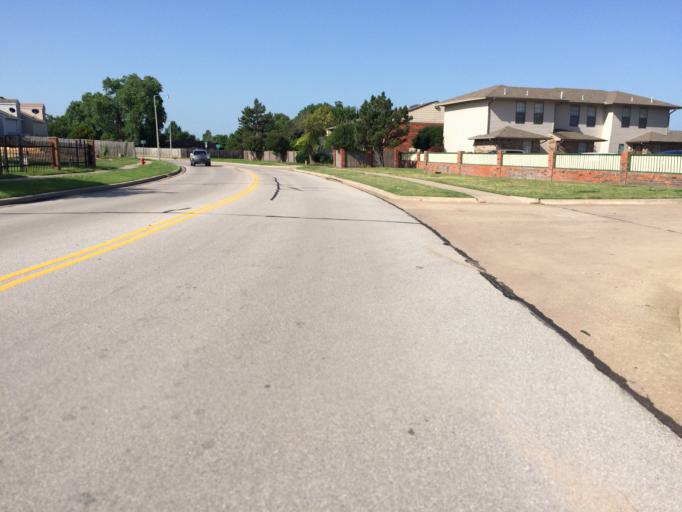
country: US
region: Oklahoma
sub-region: Cleveland County
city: Norman
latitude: 35.2309
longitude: -97.4909
